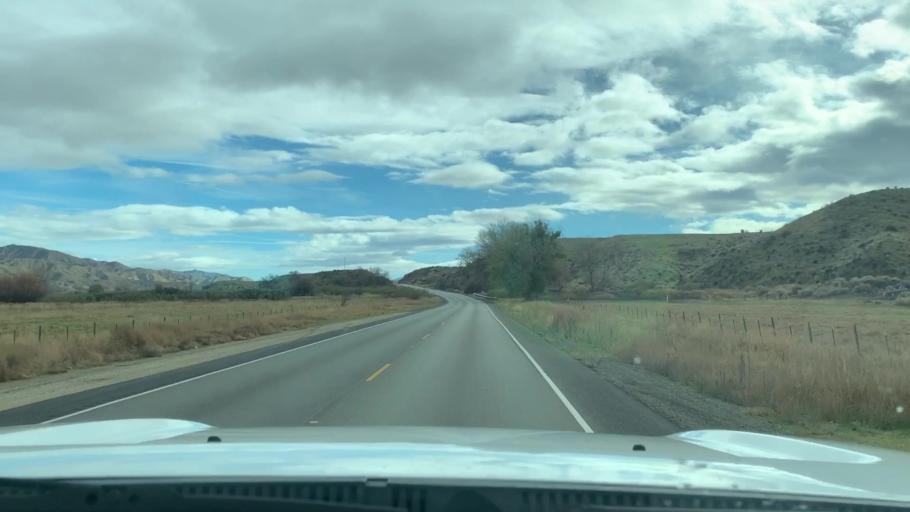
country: US
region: California
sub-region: Kern County
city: Taft Heights
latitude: 34.9867
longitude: -119.7934
